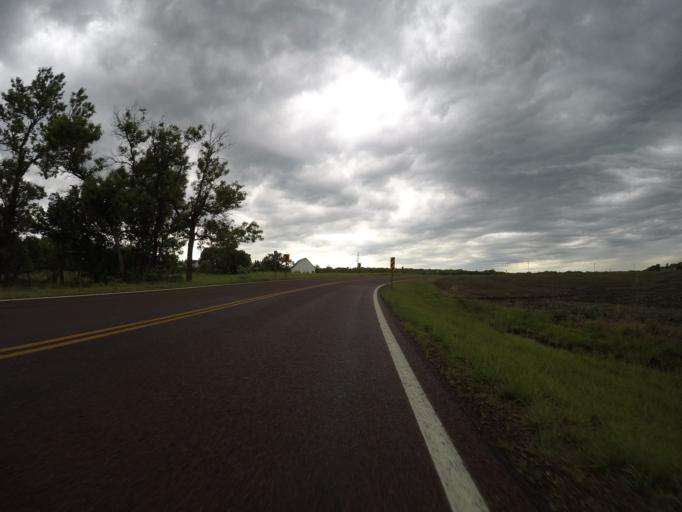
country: US
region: Kansas
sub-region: Shawnee County
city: Rossville
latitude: 38.9583
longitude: -96.0214
